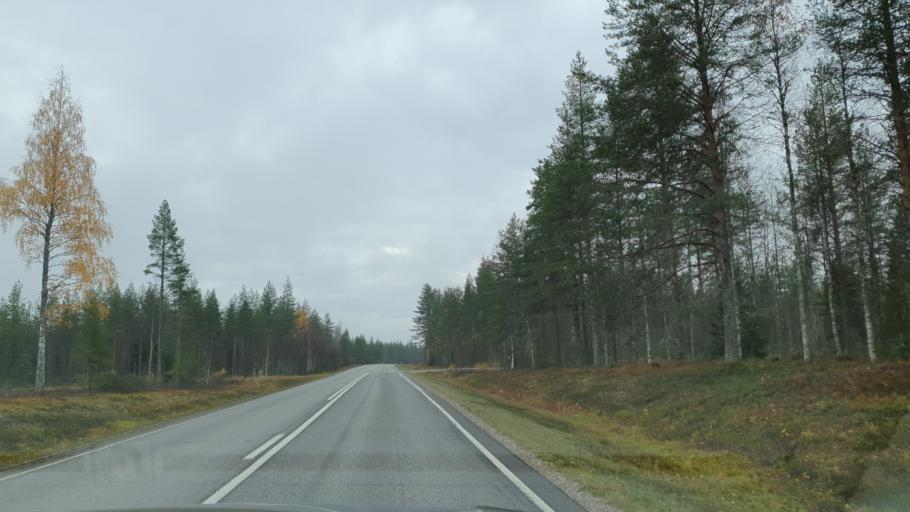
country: FI
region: Lapland
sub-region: Rovaniemi
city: Ranua
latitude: 66.0368
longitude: 26.3371
